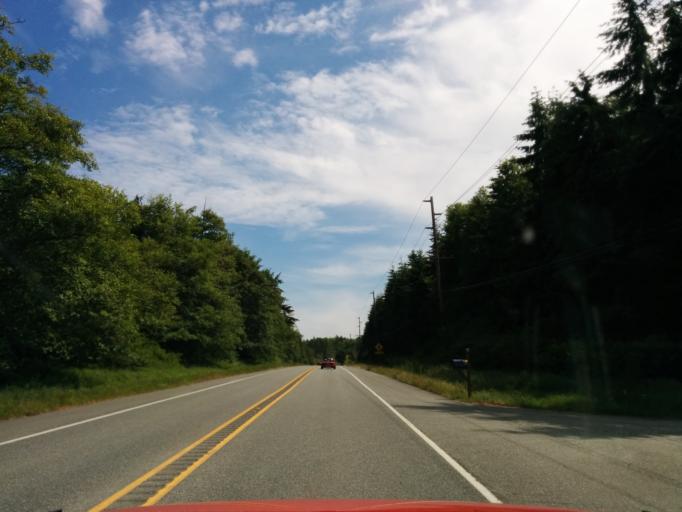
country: US
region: Washington
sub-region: Island County
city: Camano
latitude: 48.1545
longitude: -122.5967
